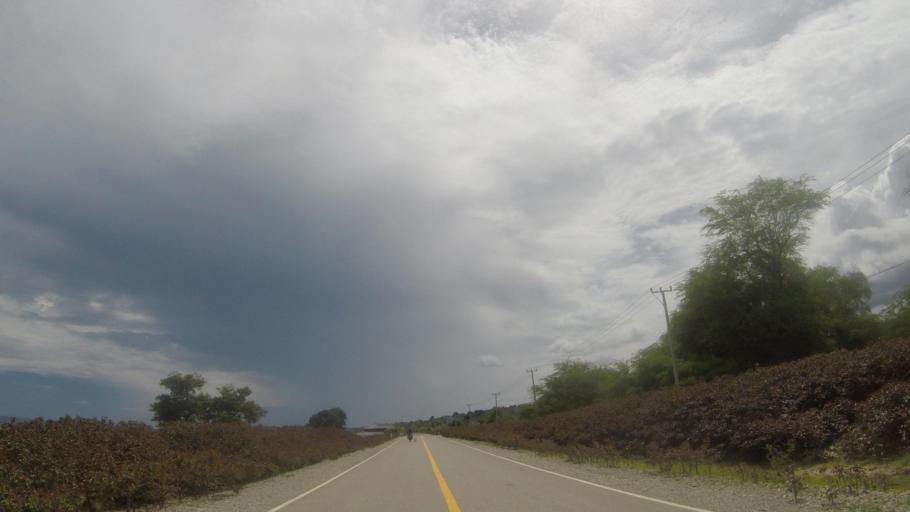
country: TL
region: Baucau
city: Baucau
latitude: -8.4527
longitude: 126.6328
